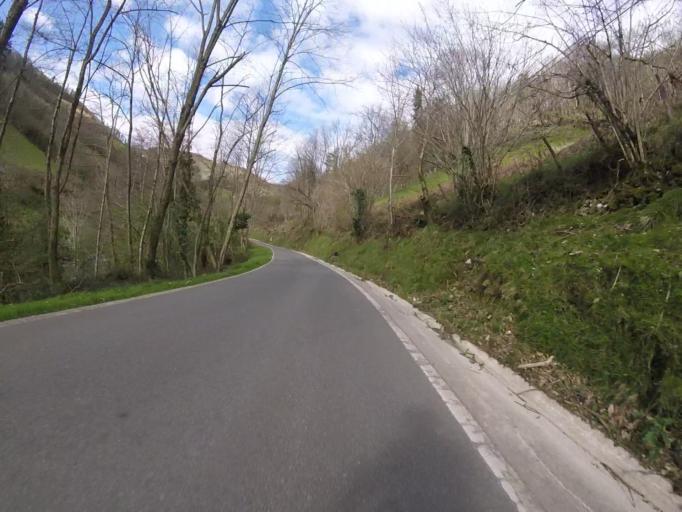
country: ES
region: Navarre
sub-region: Provincia de Navarra
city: Goizueta
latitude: 43.1689
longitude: -1.8594
